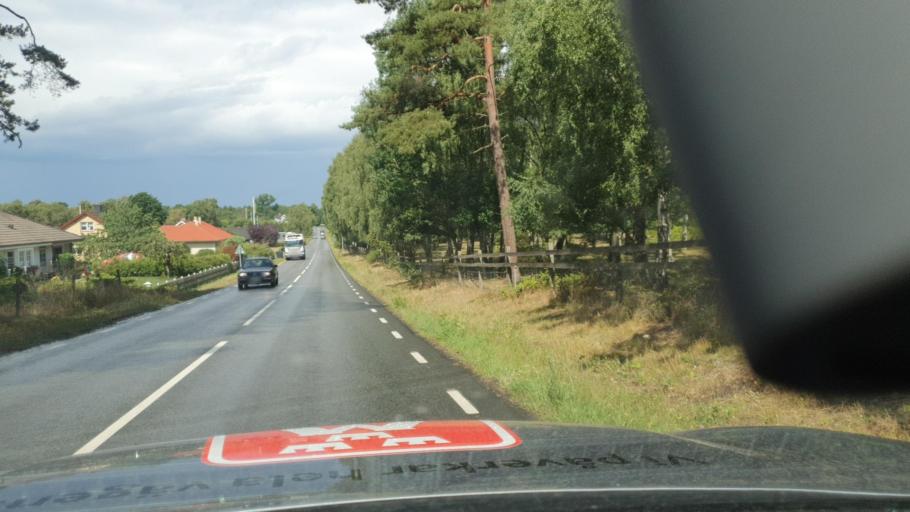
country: SE
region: Blekinge
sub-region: Solvesborgs Kommun
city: Soelvesborg
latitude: 56.0156
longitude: 14.6853
